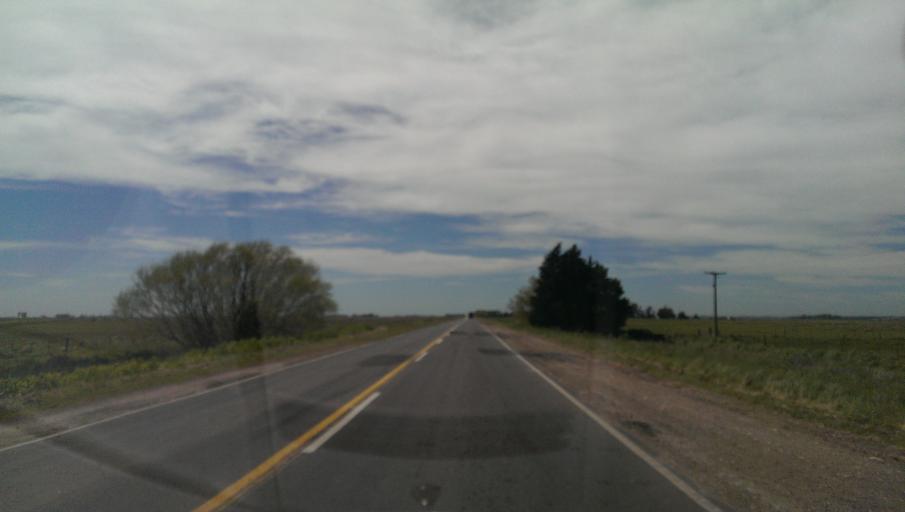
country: AR
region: Buenos Aires
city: Olavarria
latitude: -37.0347
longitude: -60.4289
